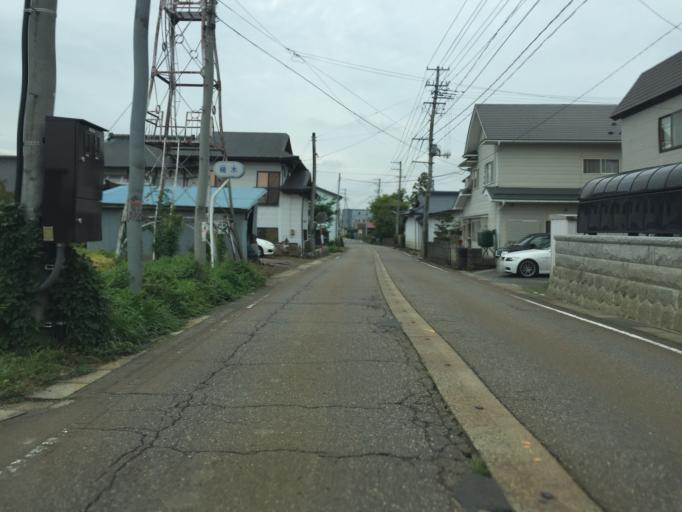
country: JP
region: Fukushima
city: Kitakata
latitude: 37.5309
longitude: 139.9314
